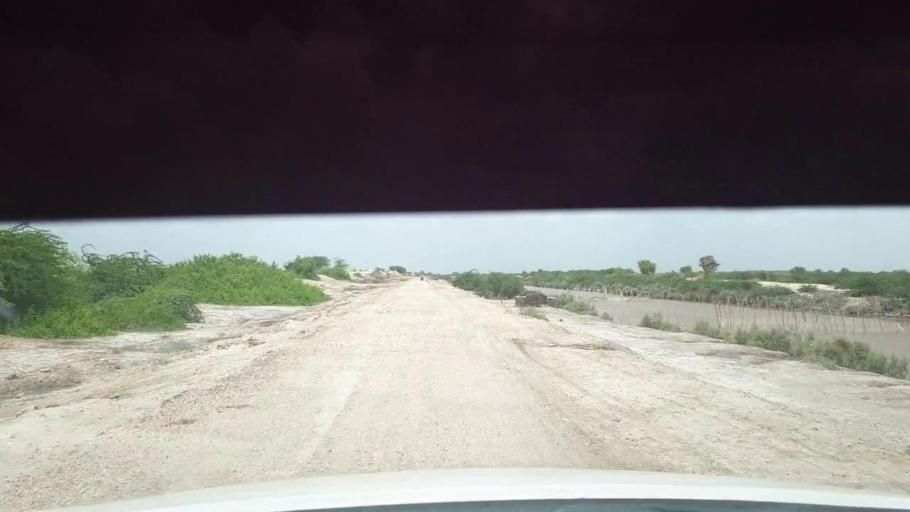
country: PK
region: Sindh
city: Kadhan
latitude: 24.5156
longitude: 69.1204
